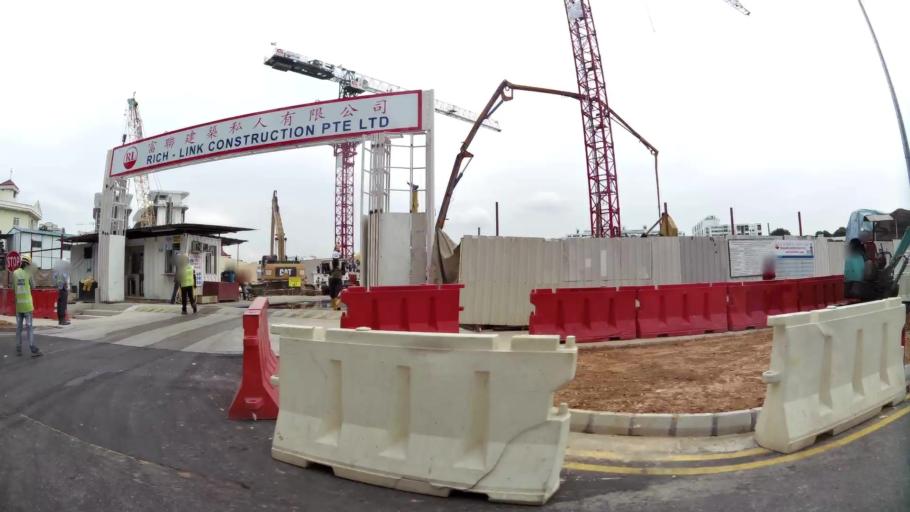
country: SG
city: Singapore
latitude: 1.3616
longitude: 103.8869
